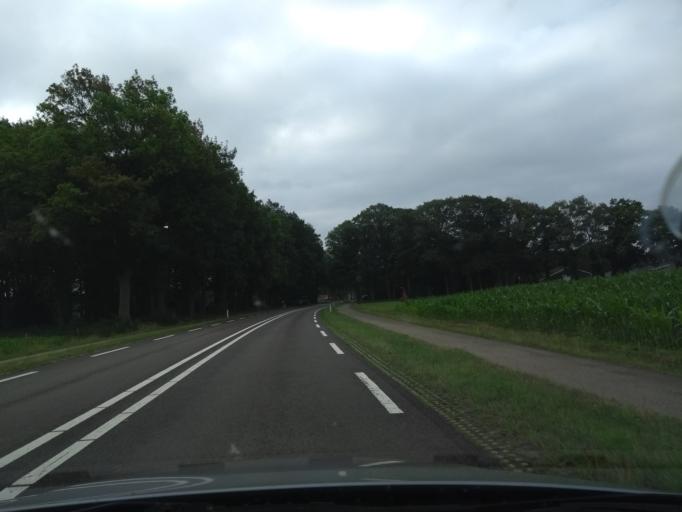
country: NL
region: Overijssel
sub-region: Gemeente Hof van Twente
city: Delden
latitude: 52.2881
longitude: 6.6691
